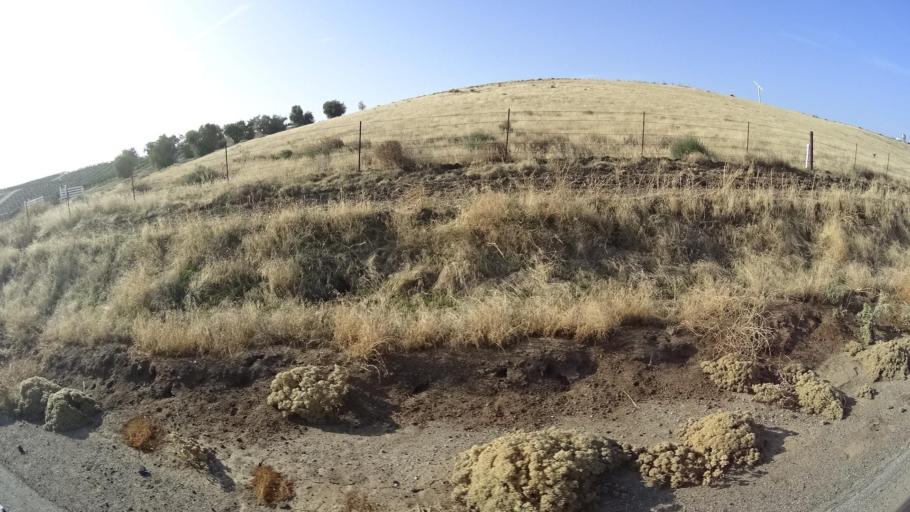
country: US
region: California
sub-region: Tulare County
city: Richgrove
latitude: 35.6439
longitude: -119.0513
